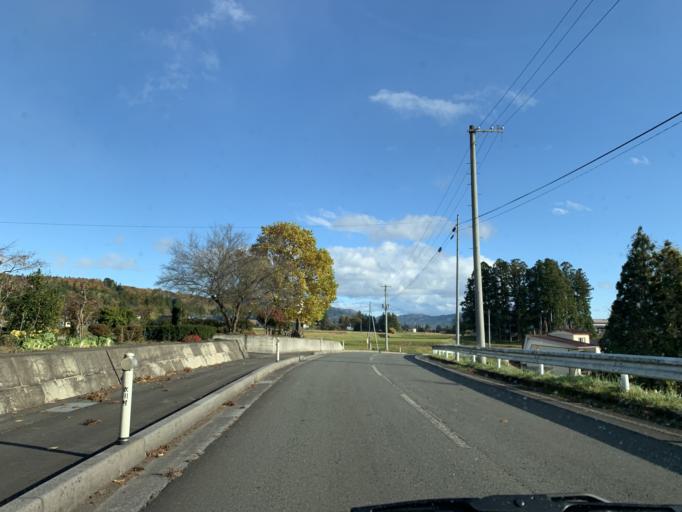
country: JP
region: Iwate
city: Ichinoseki
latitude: 39.0209
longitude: 141.0862
